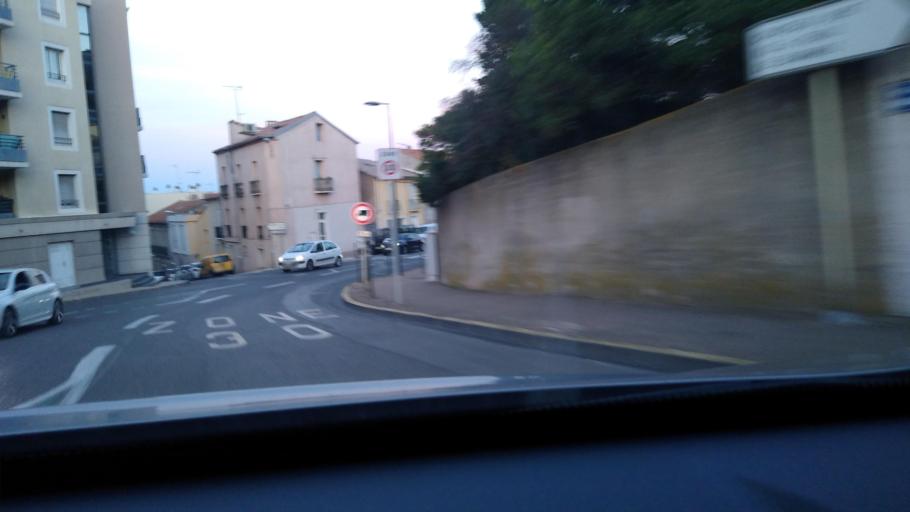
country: FR
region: Languedoc-Roussillon
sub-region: Departement de l'Herault
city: Sete
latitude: 43.4061
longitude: 3.6876
